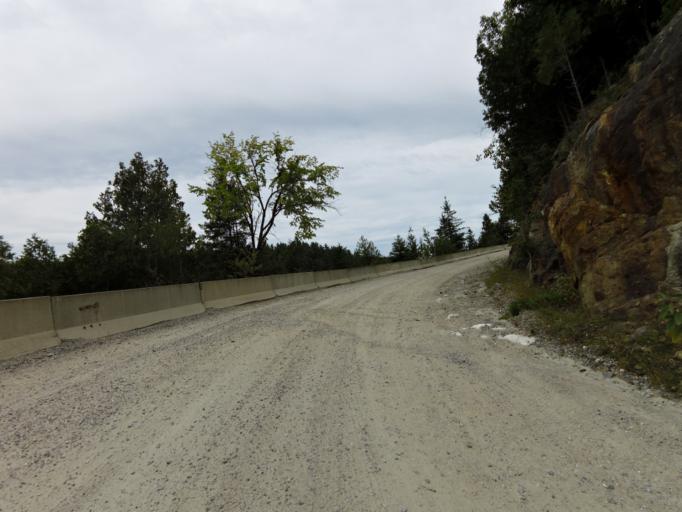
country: CA
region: Quebec
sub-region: Outaouais
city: Wakefield
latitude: 45.8109
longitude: -75.9299
